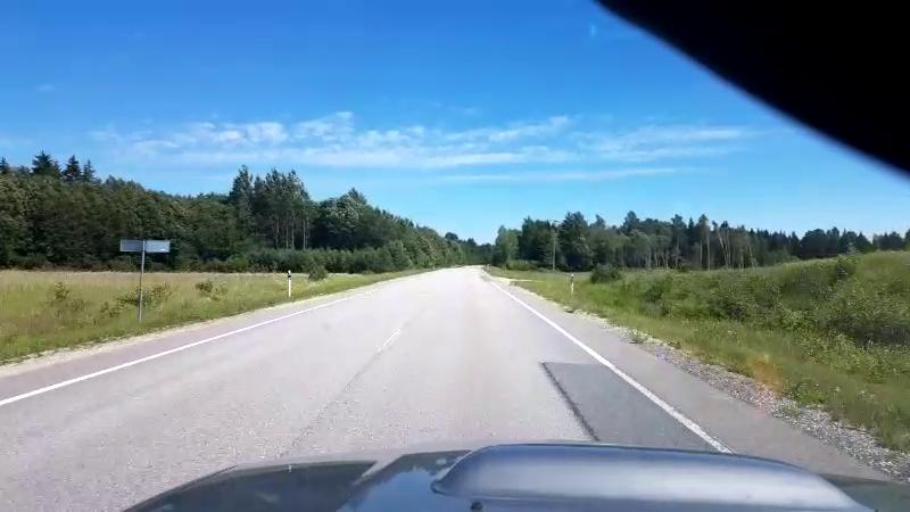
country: EE
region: Jaervamaa
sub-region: Koeru vald
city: Koeru
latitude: 58.9769
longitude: 26.1048
